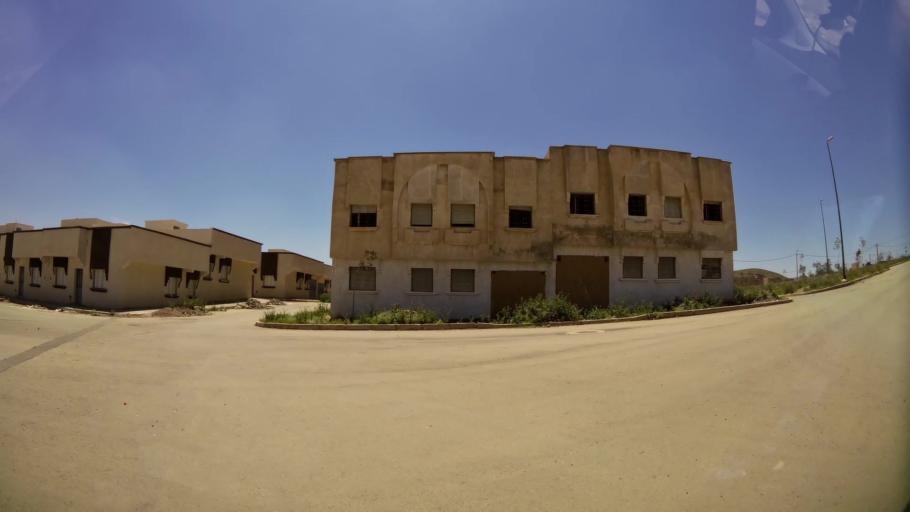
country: MA
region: Oriental
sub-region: Oujda-Angad
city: Oujda
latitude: 34.6529
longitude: -1.9475
